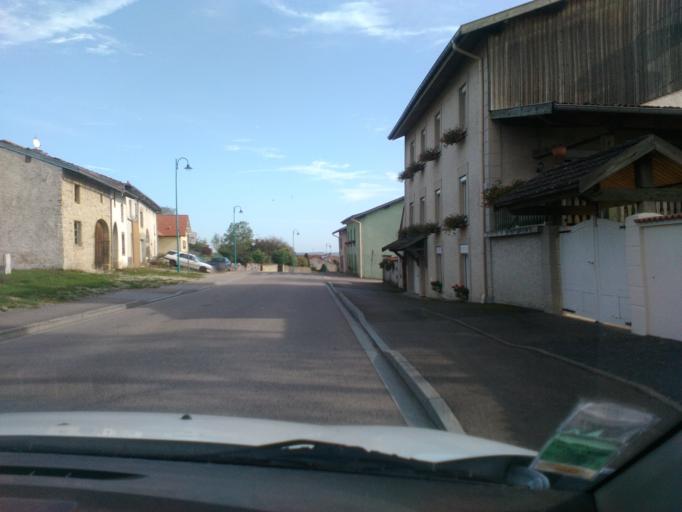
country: FR
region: Lorraine
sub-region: Departement des Vosges
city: Rambervillers
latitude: 48.3507
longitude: 6.5391
